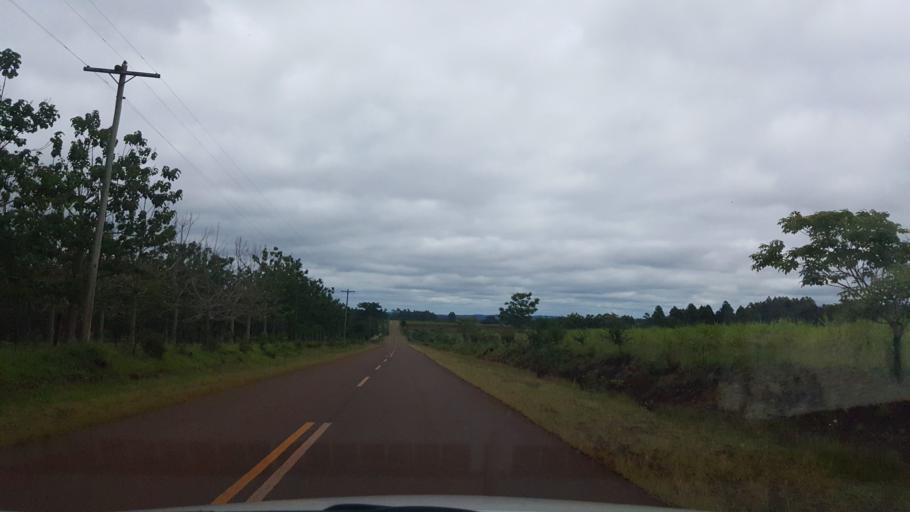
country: AR
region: Misiones
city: Ruiz de Montoya
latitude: -26.9686
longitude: -55.0659
